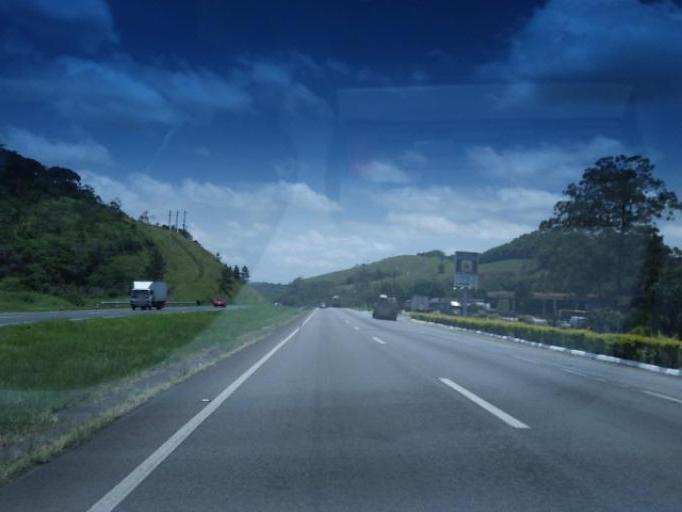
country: BR
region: Sao Paulo
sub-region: Juquia
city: Juquia
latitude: -24.3611
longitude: -47.6892
